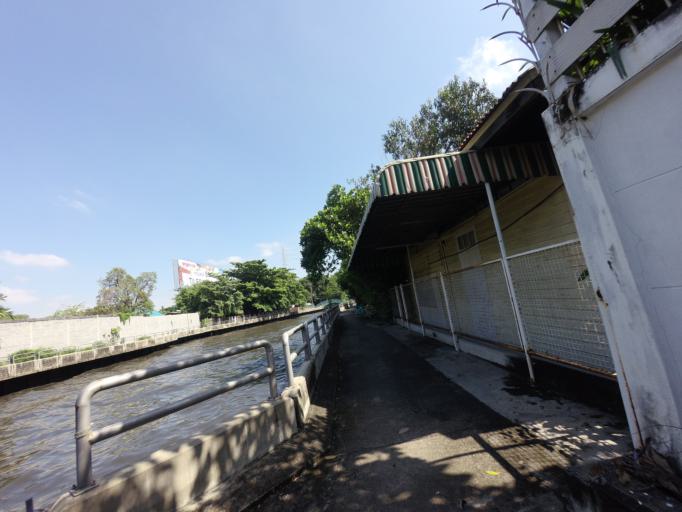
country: TH
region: Bangkok
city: Watthana
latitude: 13.7469
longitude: 100.6002
